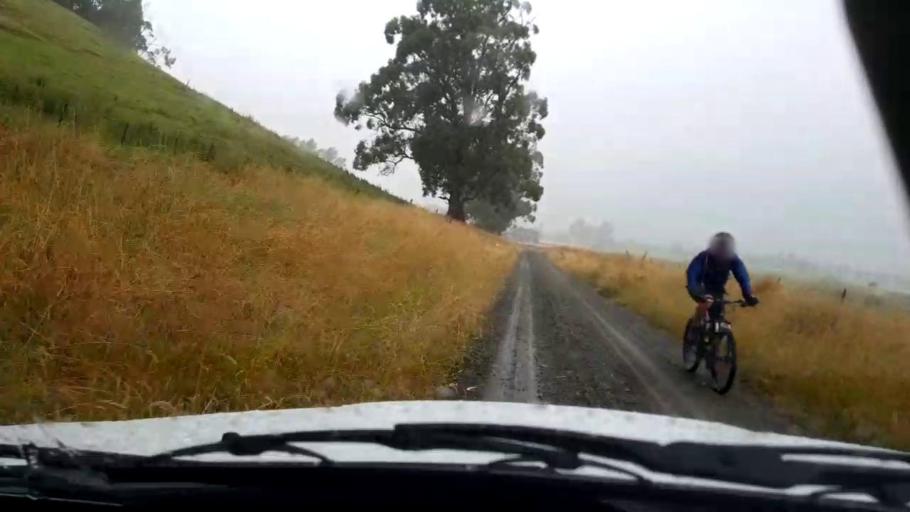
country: NZ
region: Canterbury
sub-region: Timaru District
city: Pleasant Point
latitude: -44.1938
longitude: 171.1042
